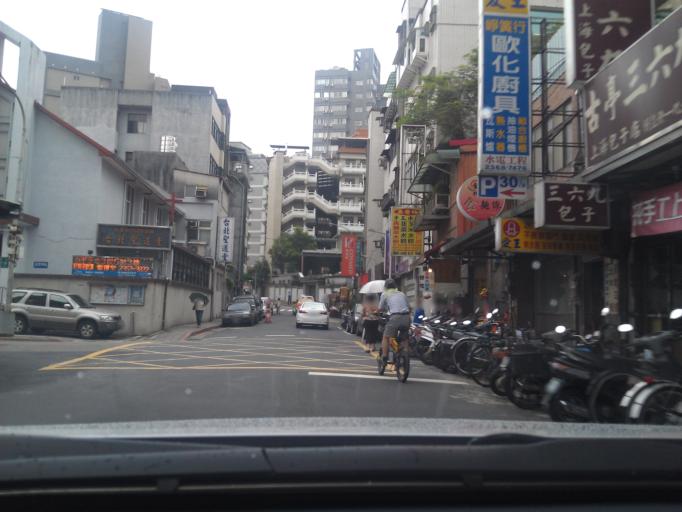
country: TW
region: Taipei
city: Taipei
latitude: 25.0243
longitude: 121.5218
